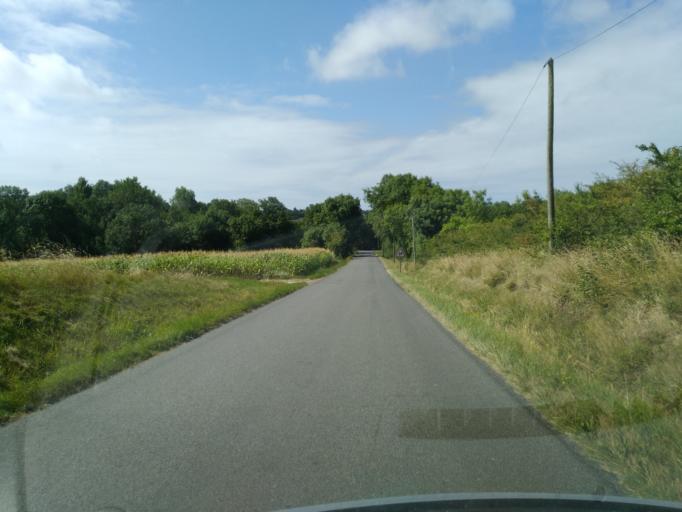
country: FR
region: Poitou-Charentes
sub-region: Departement de la Charente-Maritime
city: Breuillet
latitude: 45.6843
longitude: -1.0787
